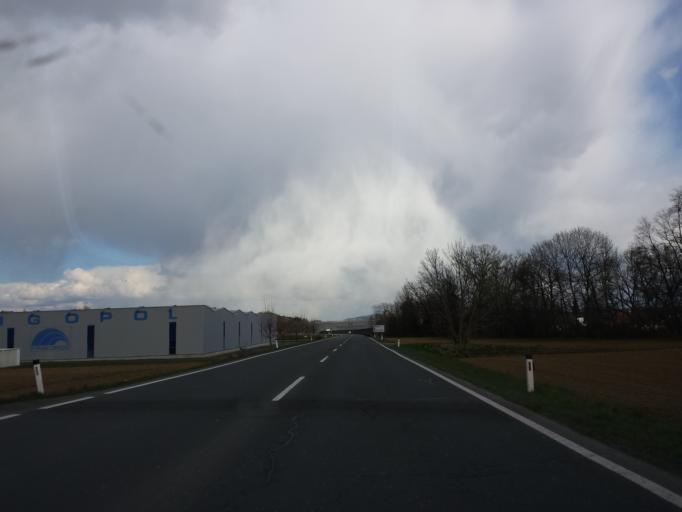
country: AT
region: Styria
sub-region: Politischer Bezirk Deutschlandsberg
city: Deutschlandsberg
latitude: 46.8312
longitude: 15.2500
